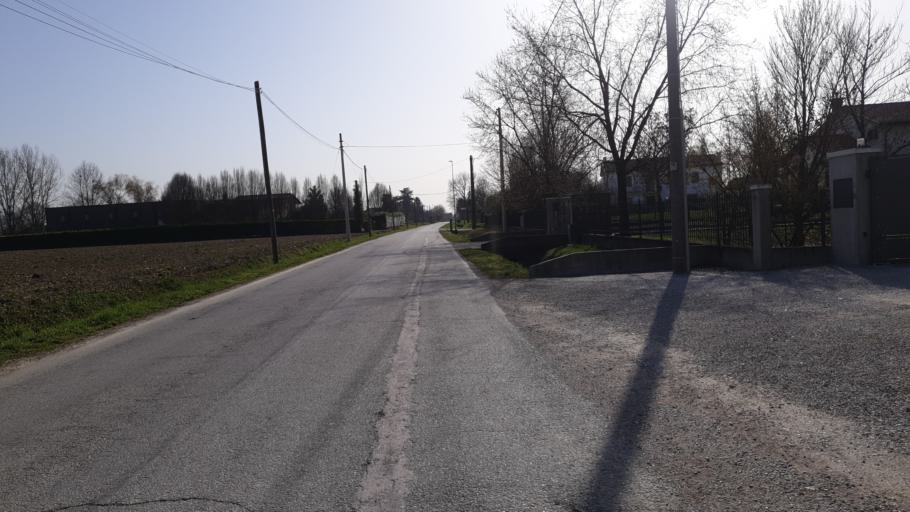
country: IT
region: Veneto
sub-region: Provincia di Padova
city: Cavino
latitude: 45.5108
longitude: 11.8818
